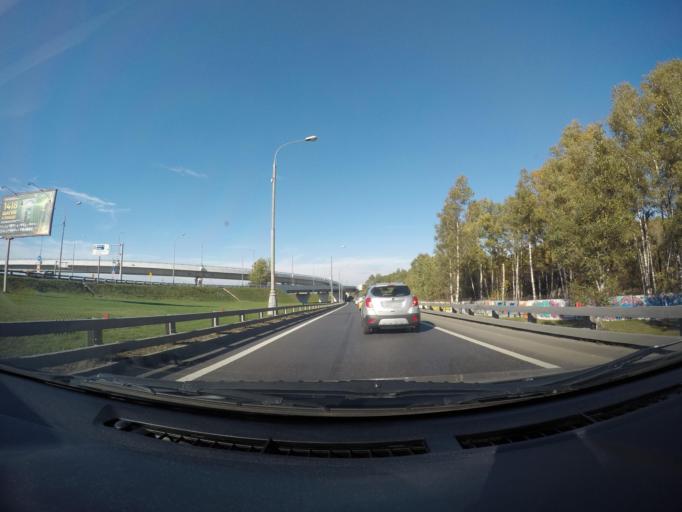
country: RU
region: Moscow
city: Zhulebino
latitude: 55.6858
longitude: 37.8351
